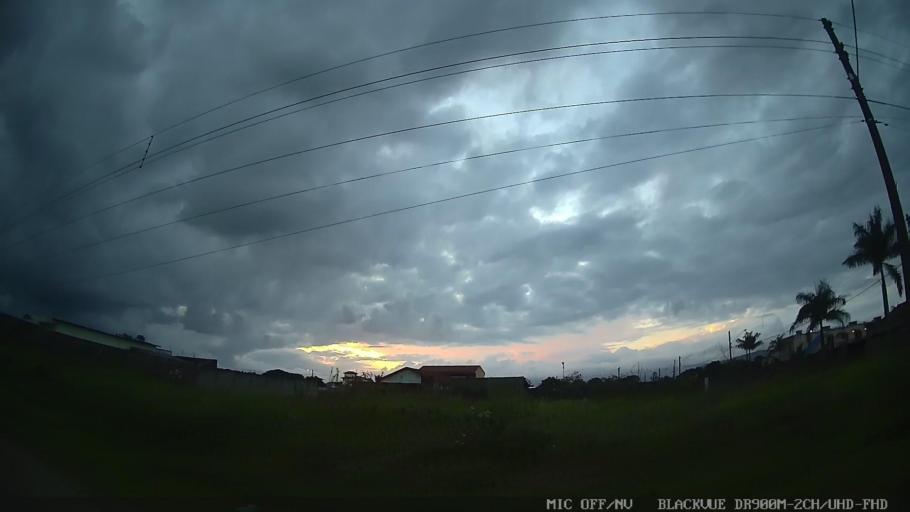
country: BR
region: Sao Paulo
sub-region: Itanhaem
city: Itanhaem
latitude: -24.1874
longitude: -46.8317
